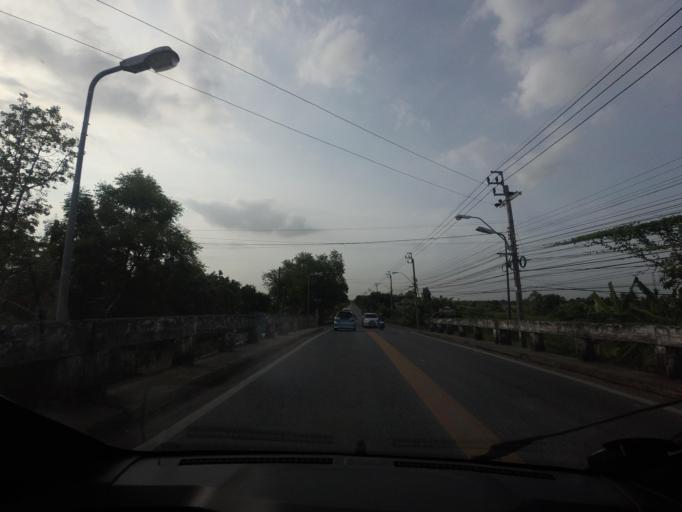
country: TH
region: Bangkok
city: Nong Chok
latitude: 13.8285
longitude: 100.8703
